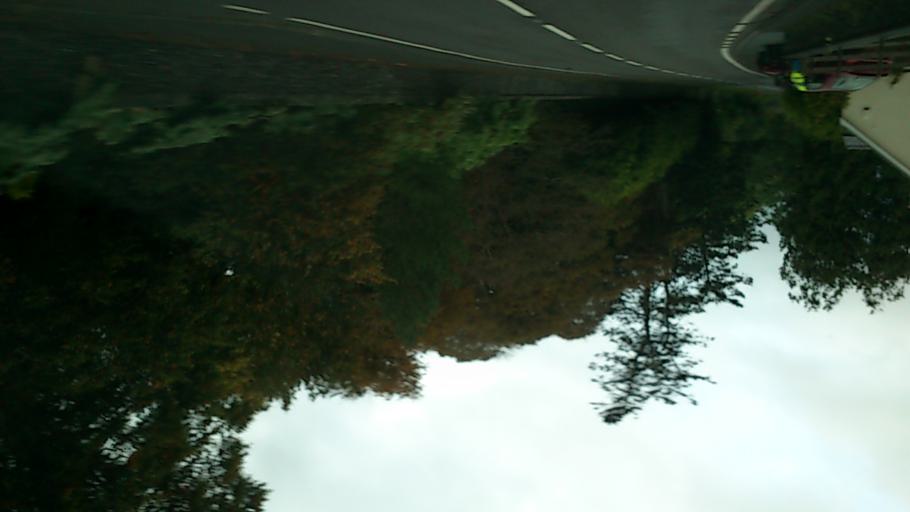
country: GB
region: Wales
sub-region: Sir Powys
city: Machynlleth
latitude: 52.5477
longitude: -3.9348
